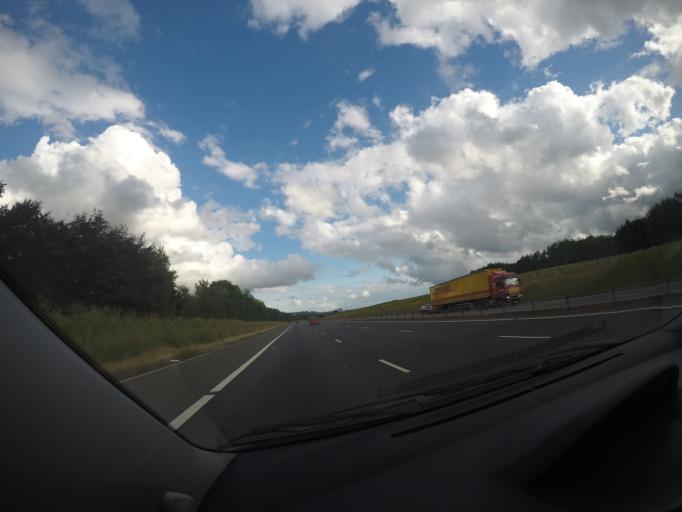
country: GB
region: Scotland
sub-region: Dumfries and Galloway
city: Lockerbie
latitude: 55.1701
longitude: -3.3927
